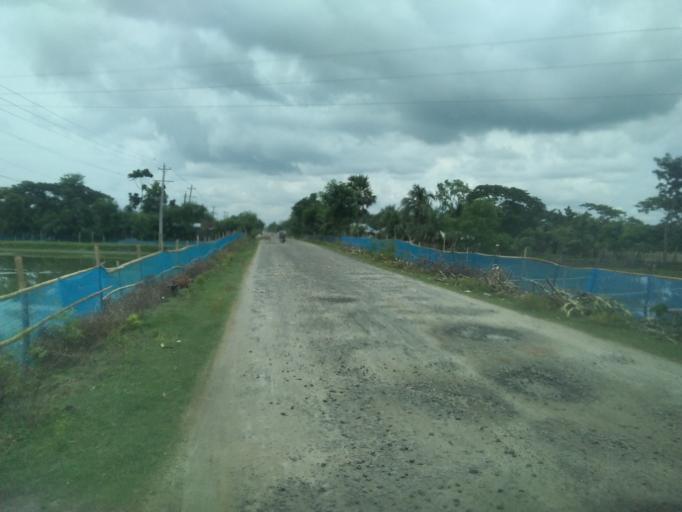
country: IN
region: West Bengal
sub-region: North 24 Parganas
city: Gosaba
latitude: 22.2664
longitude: 89.1725
